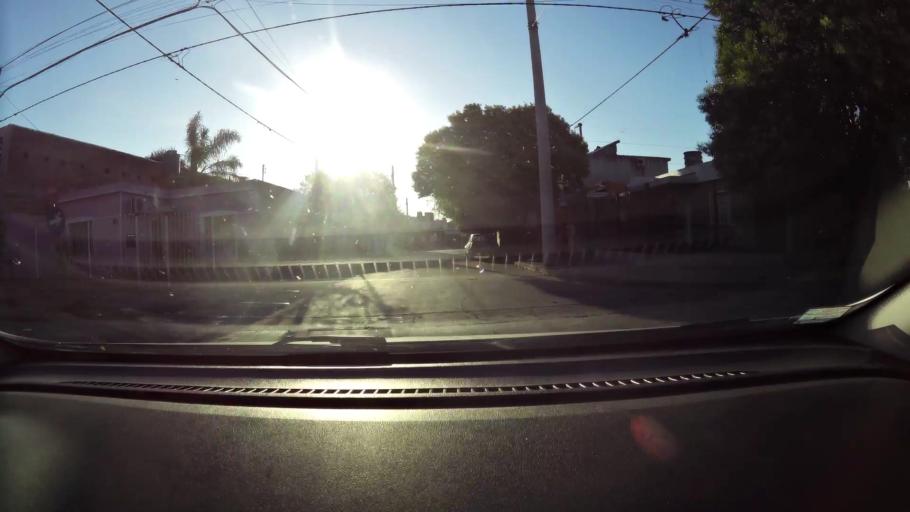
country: AR
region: Cordoba
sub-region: Departamento de Capital
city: Cordoba
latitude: -31.3740
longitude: -64.1984
